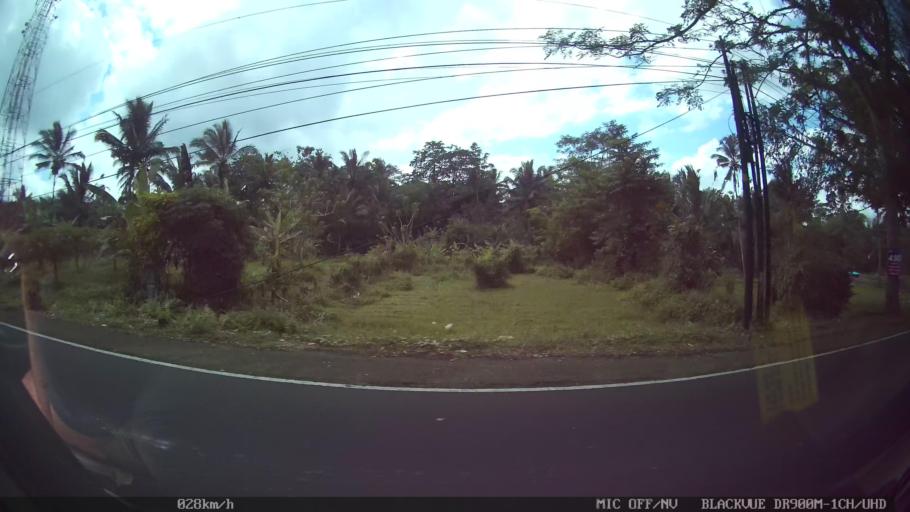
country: ID
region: Bali
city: Pergan
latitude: -8.4195
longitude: 115.1991
